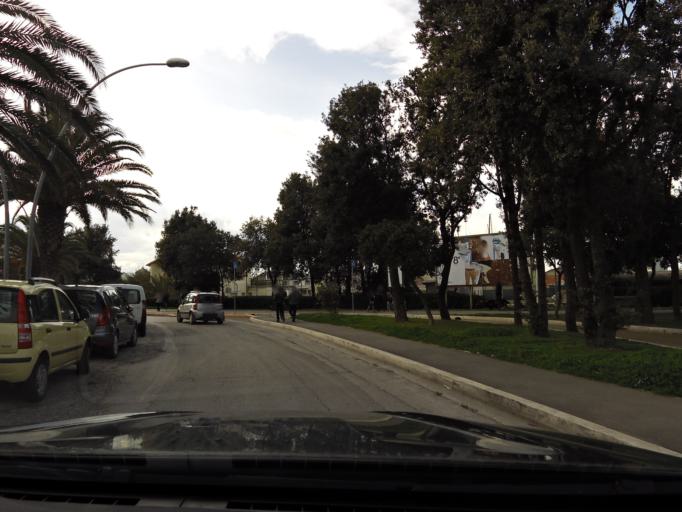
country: IT
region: The Marches
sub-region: Provincia di Macerata
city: Portocivitanova
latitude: 43.3093
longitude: 13.7331
